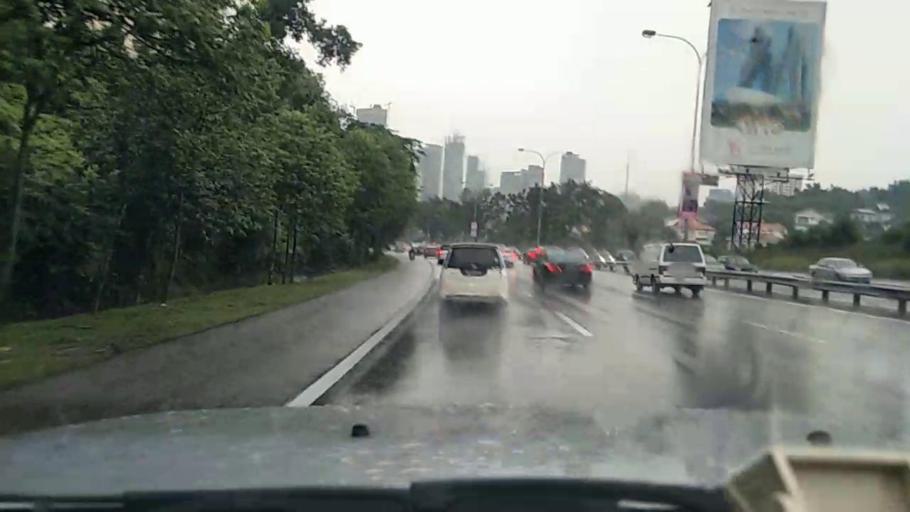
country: MY
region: Kuala Lumpur
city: Kuala Lumpur
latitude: 3.1114
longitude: 101.6879
